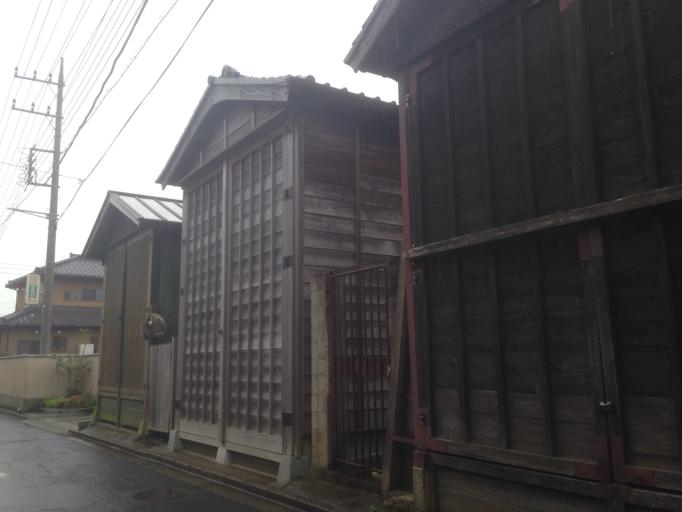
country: JP
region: Chiba
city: Sawara
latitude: 35.8873
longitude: 140.4956
